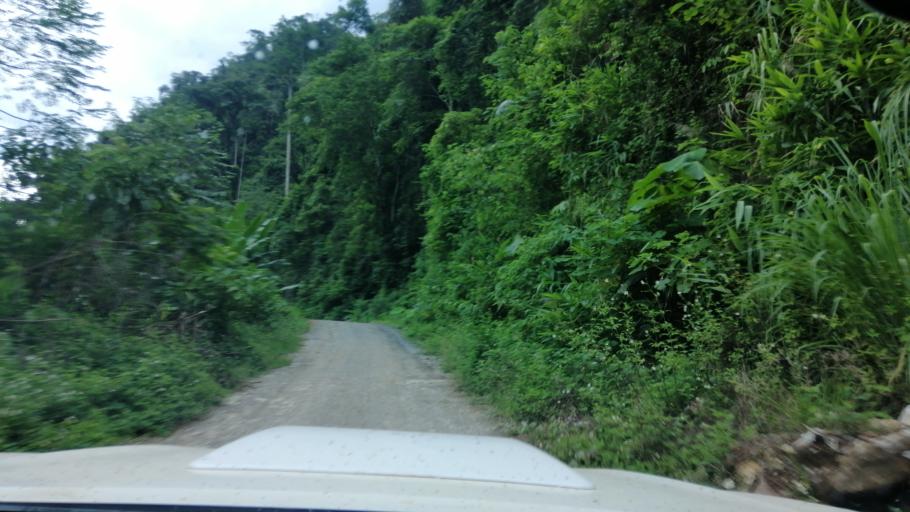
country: LA
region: Xiagnabouli
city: Sainyabuli
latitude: 19.1947
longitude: 101.7753
